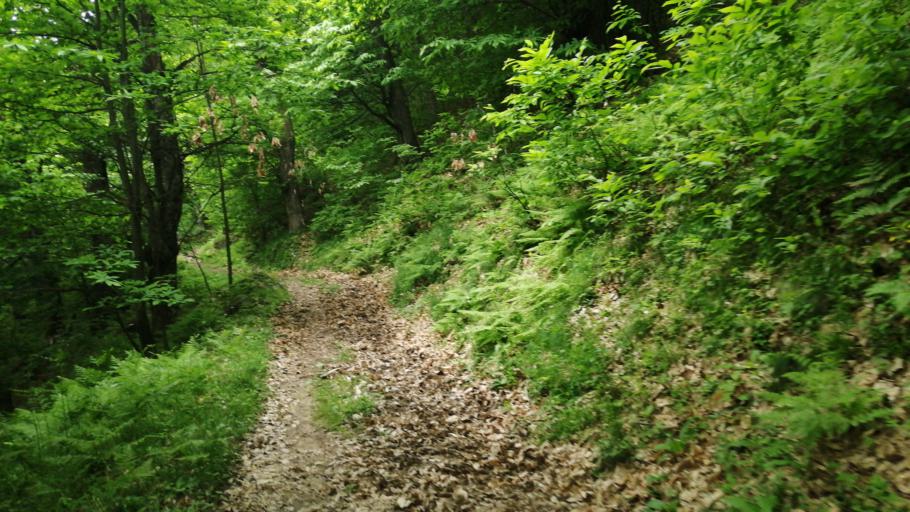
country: IT
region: Piedmont
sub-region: Provincia di Cuneo
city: Montaldo di Mondovi
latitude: 44.3147
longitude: 7.8639
